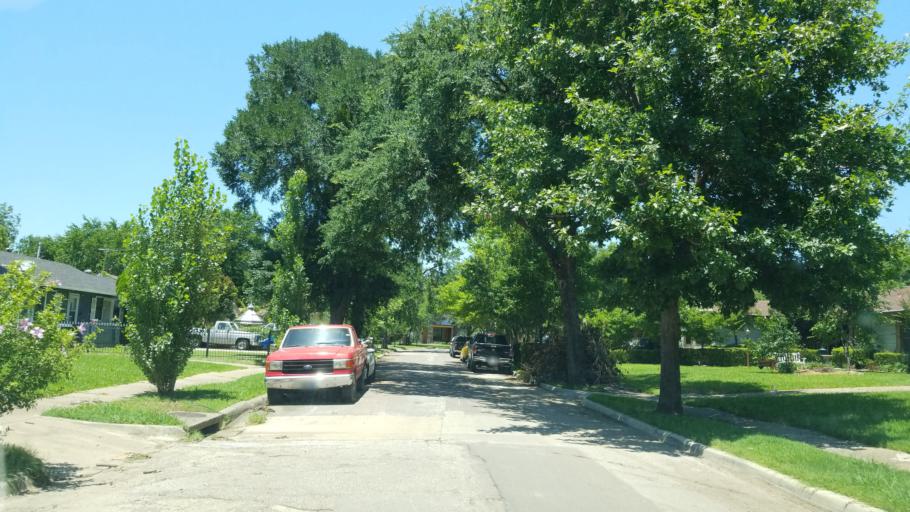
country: US
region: Texas
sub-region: Dallas County
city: University Park
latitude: 32.8753
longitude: -96.8514
